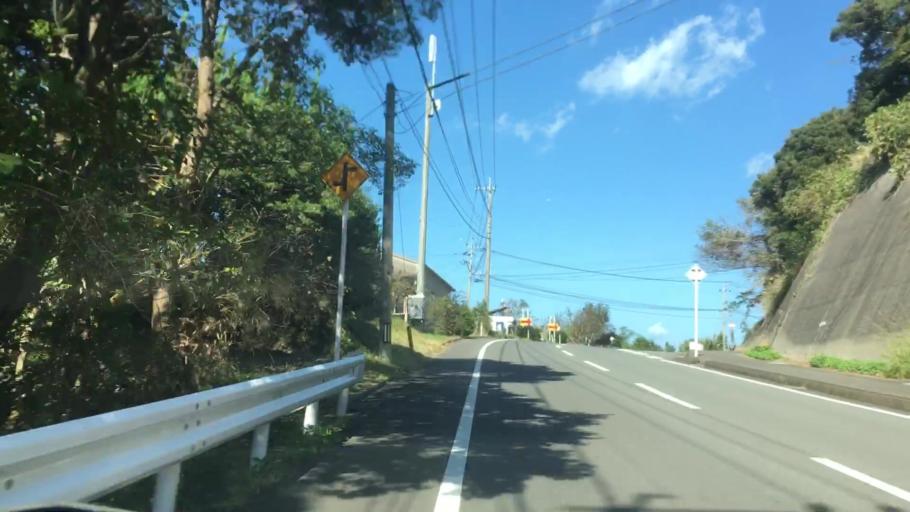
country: JP
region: Nagasaki
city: Sasebo
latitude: 33.0052
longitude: 129.6571
